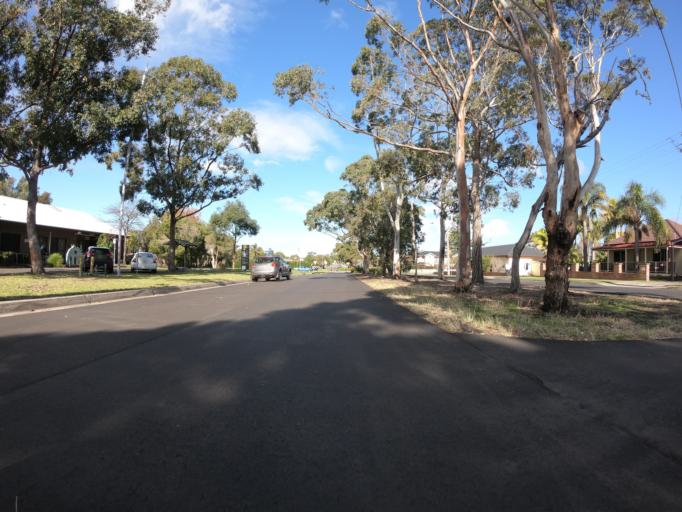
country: AU
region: New South Wales
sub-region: Wollongong
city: East Corrimal
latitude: -34.3682
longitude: 150.9166
